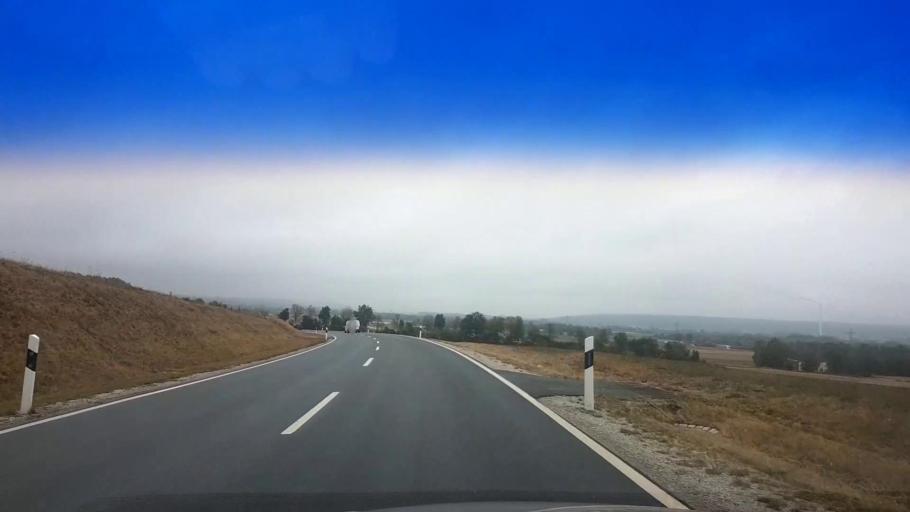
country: DE
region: Bavaria
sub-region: Upper Franconia
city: Buttenheim
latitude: 49.7955
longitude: 11.0353
